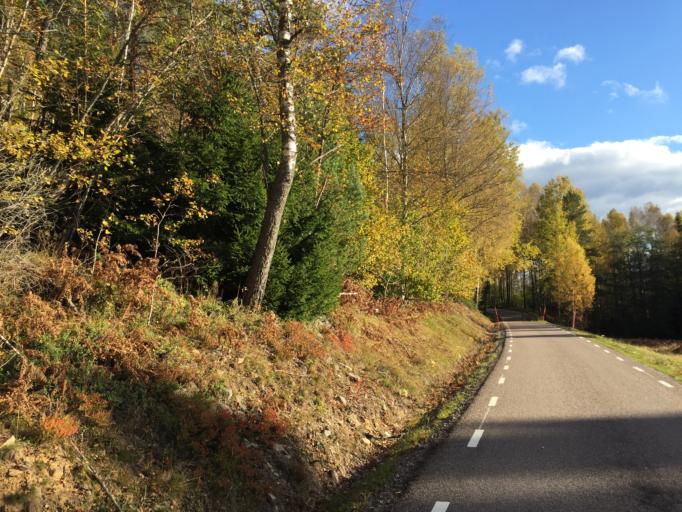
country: SE
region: OErebro
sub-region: Orebro Kommun
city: Odensbacken
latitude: 58.9683
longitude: 15.6494
